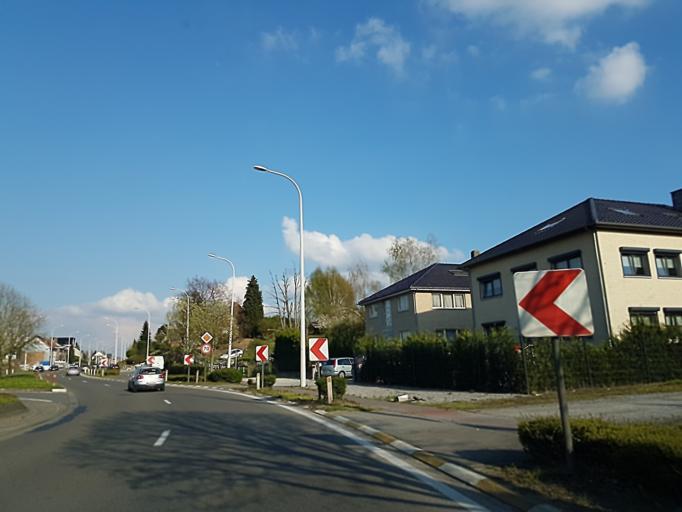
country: BE
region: Flanders
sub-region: Provincie Vlaams-Brabant
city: Dilbeek
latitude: 50.8400
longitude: 4.2205
